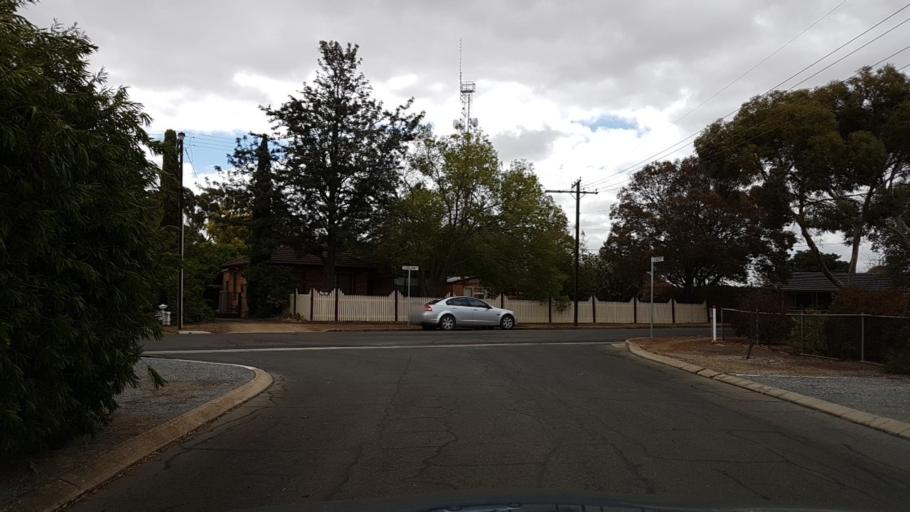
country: AU
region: South Australia
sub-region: Gawler
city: Gawler
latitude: -34.6034
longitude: 138.7612
